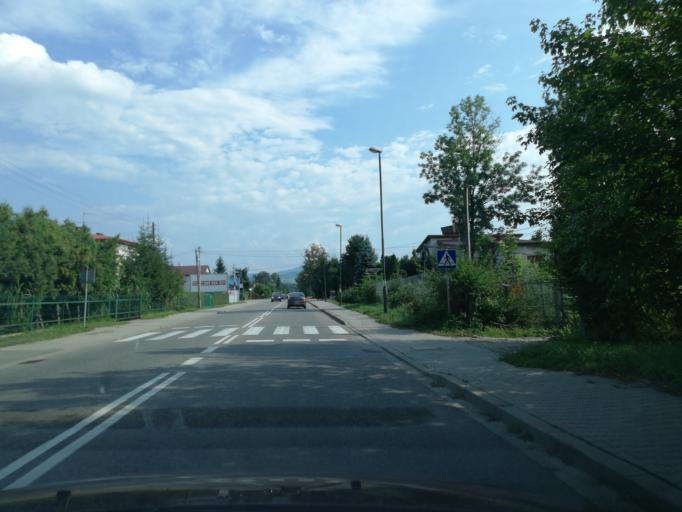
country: PL
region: Lesser Poland Voivodeship
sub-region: Powiat nowosadecki
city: Nawojowa
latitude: 49.5746
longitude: 20.7330
